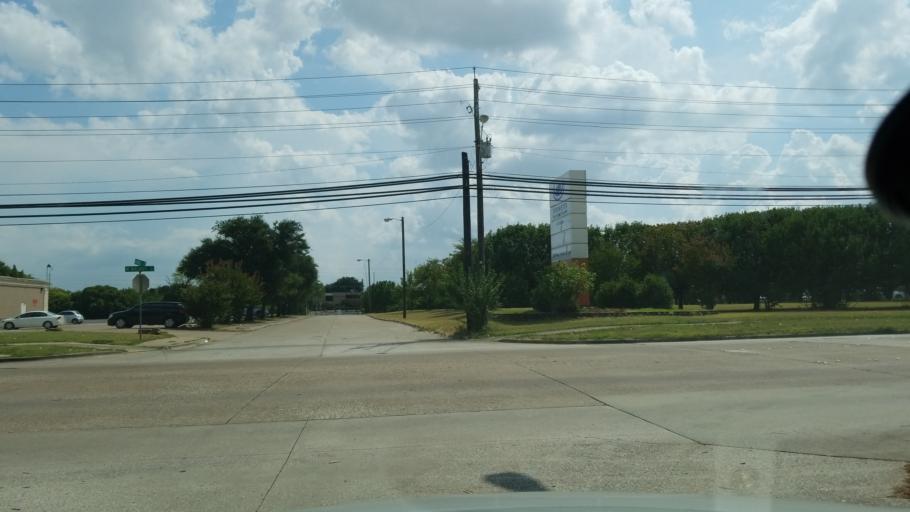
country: US
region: Texas
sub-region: Dallas County
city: Garland
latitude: 32.9168
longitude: -96.6692
